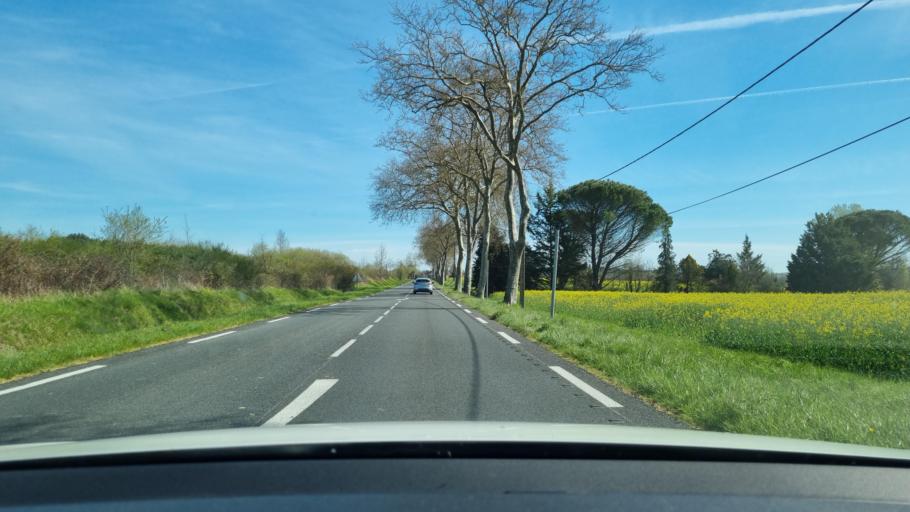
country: FR
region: Midi-Pyrenees
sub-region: Departement du Gers
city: Lombez
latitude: 43.3957
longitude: 0.7902
